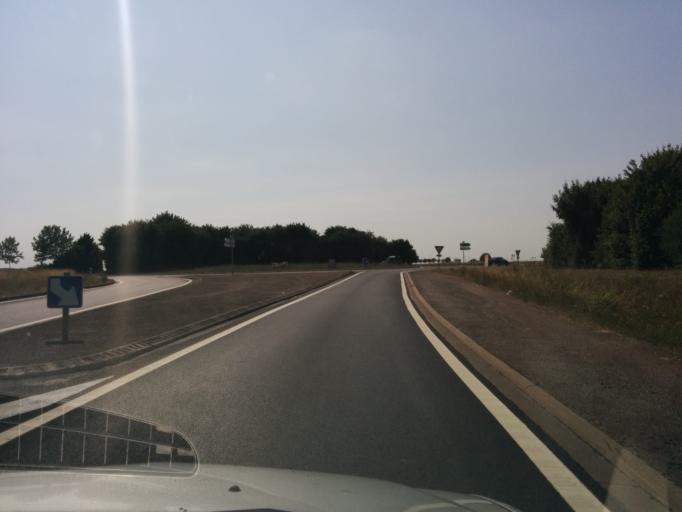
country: FR
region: Poitou-Charentes
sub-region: Departement de la Vienne
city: Neuville-de-Poitou
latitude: 46.7145
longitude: 0.2193
